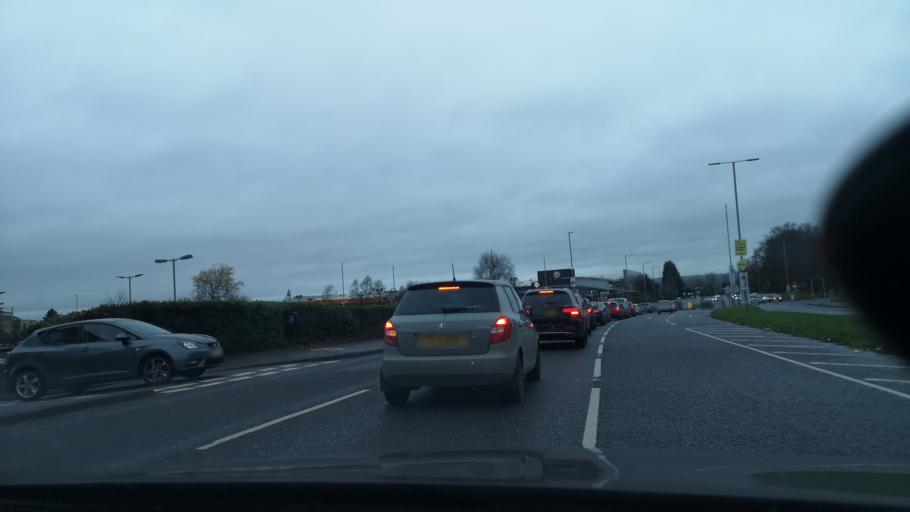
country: GB
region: Northern Ireland
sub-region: Castlereagh District
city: Castlereagh
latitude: 54.5632
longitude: -5.9077
